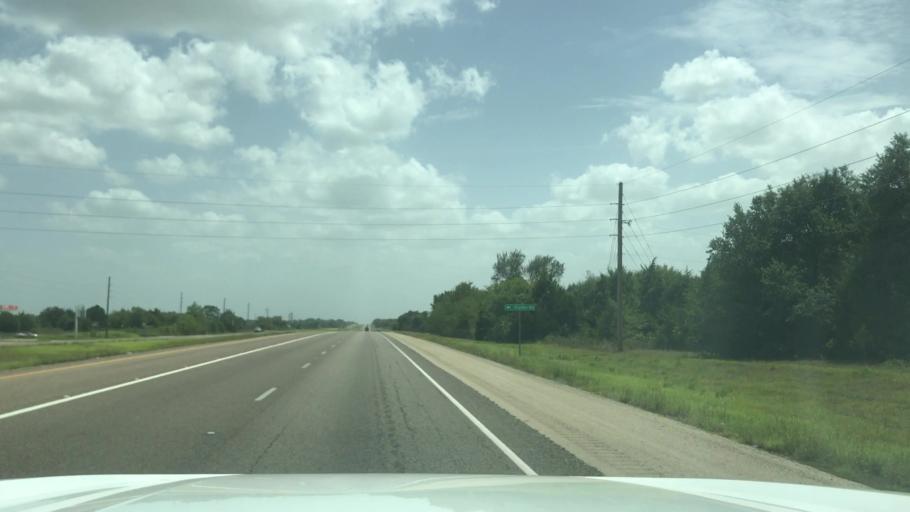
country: US
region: Texas
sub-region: Robertson County
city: Calvert
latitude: 31.0819
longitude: -96.7138
